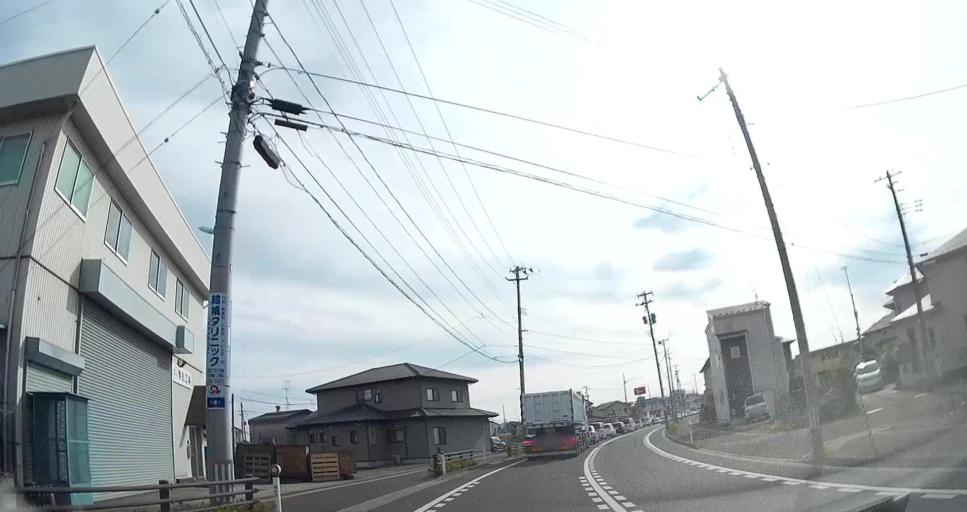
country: JP
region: Miyagi
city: Sendai
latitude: 38.2176
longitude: 140.9304
